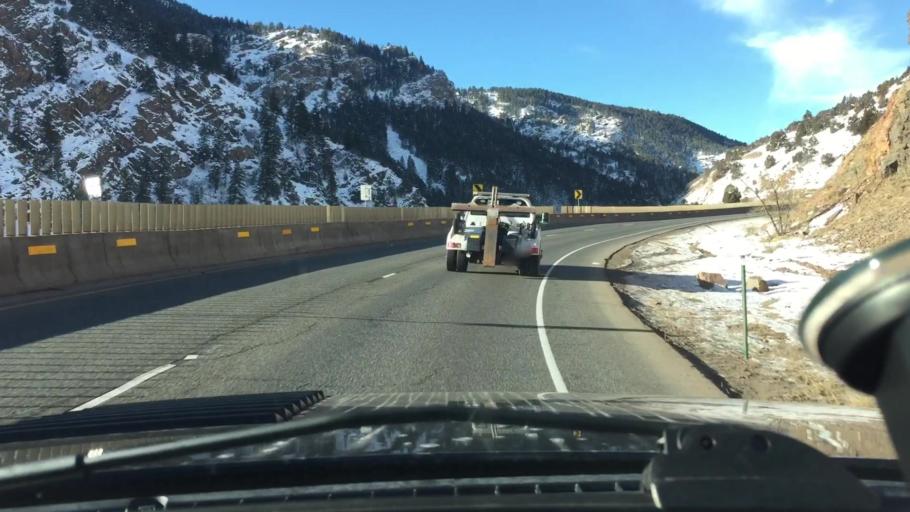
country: US
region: Colorado
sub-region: Jefferson County
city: Indian Hills
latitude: 39.6214
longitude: -105.1966
